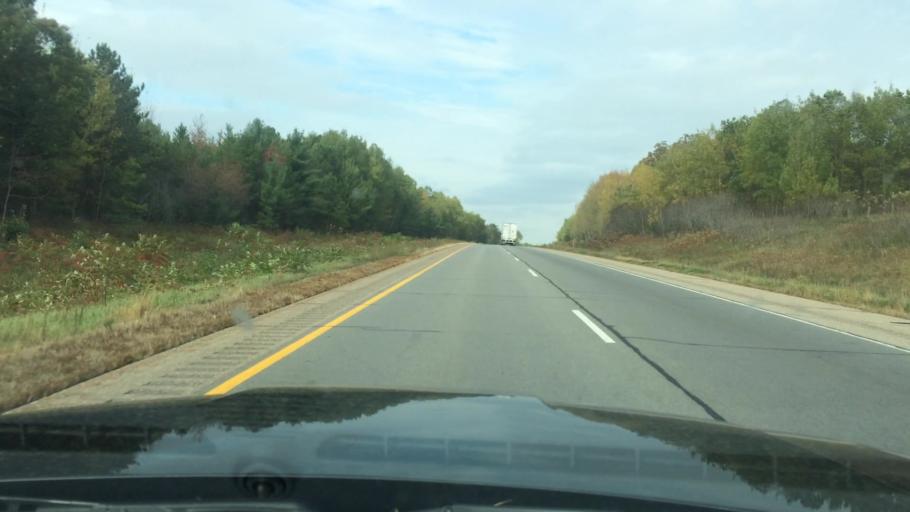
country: US
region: Wisconsin
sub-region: Marathon County
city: Mosinee
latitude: 44.7020
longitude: -89.6509
